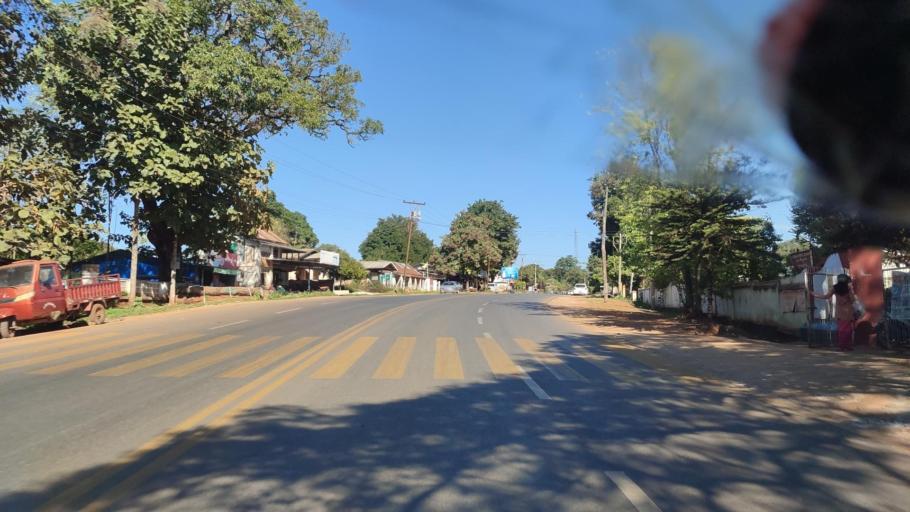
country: MM
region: Mandalay
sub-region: Pyin Oo Lwin District
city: Pyin Oo Lwin
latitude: 22.0937
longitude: 96.5897
